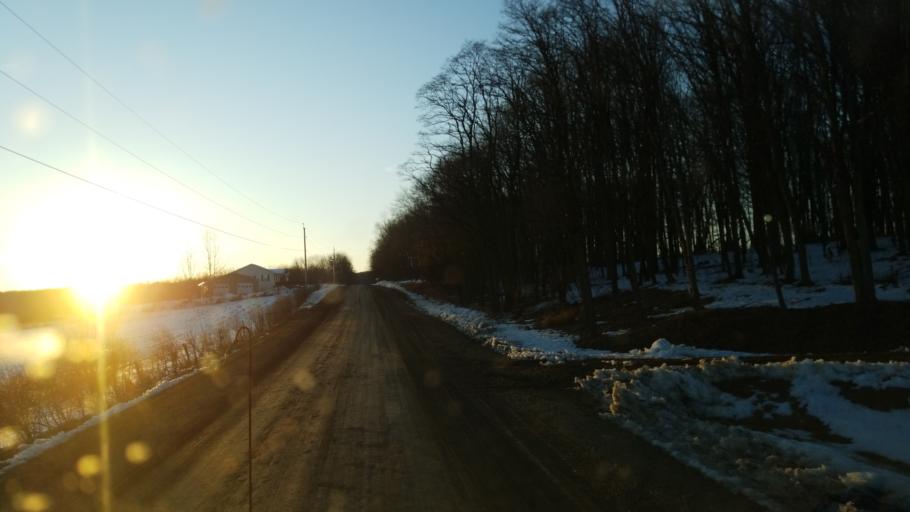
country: US
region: Pennsylvania
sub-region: Tioga County
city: Westfield
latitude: 42.0393
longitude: -77.6128
